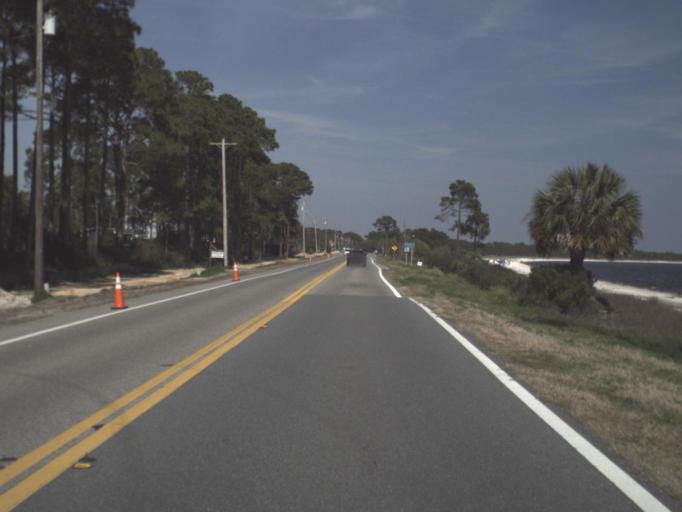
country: US
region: Florida
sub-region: Franklin County
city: Carrabelle
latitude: 29.8271
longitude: -84.6969
